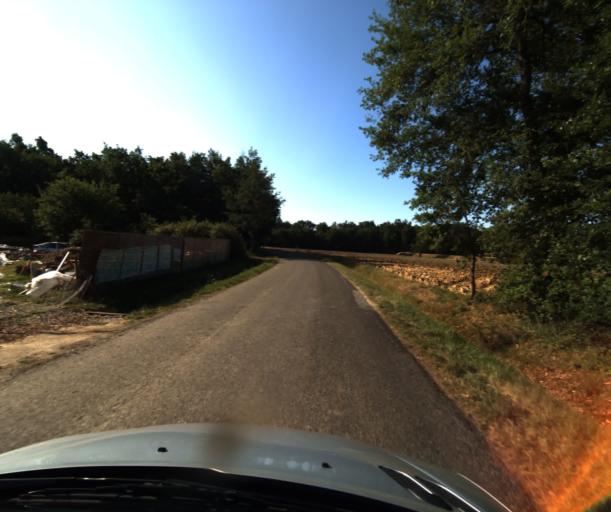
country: FR
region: Midi-Pyrenees
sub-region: Departement du Tarn-et-Garonne
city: Saint-Porquier
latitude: 44.0655
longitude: 1.2047
